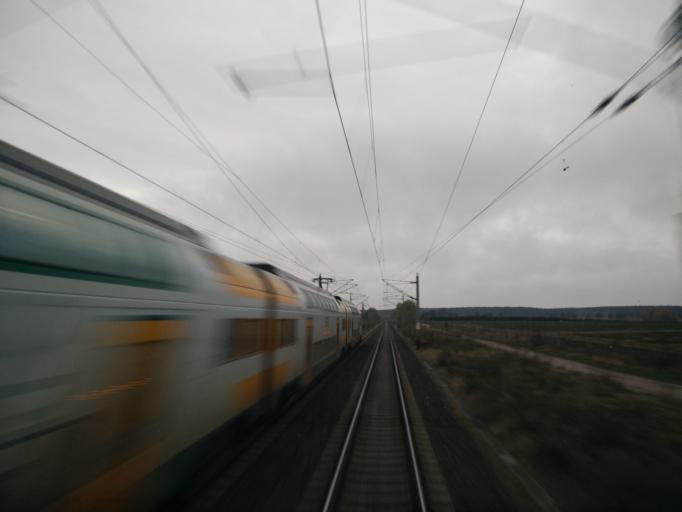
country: DE
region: Brandenburg
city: Kyritz
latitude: 52.8863
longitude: 12.3666
